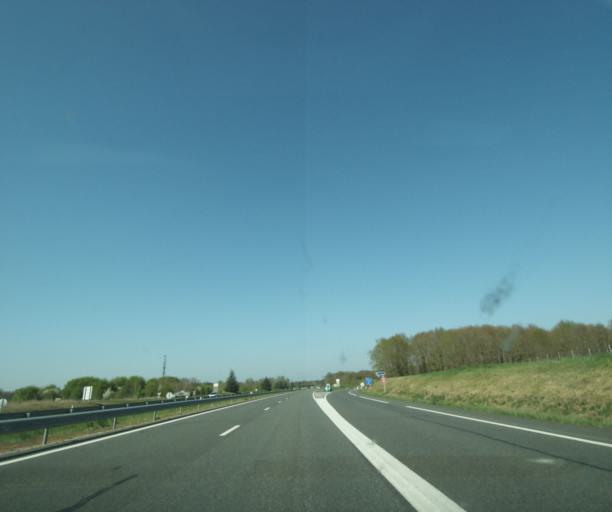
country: FR
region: Centre
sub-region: Departement du Loiret
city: Vimory
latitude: 47.9736
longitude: 2.6728
